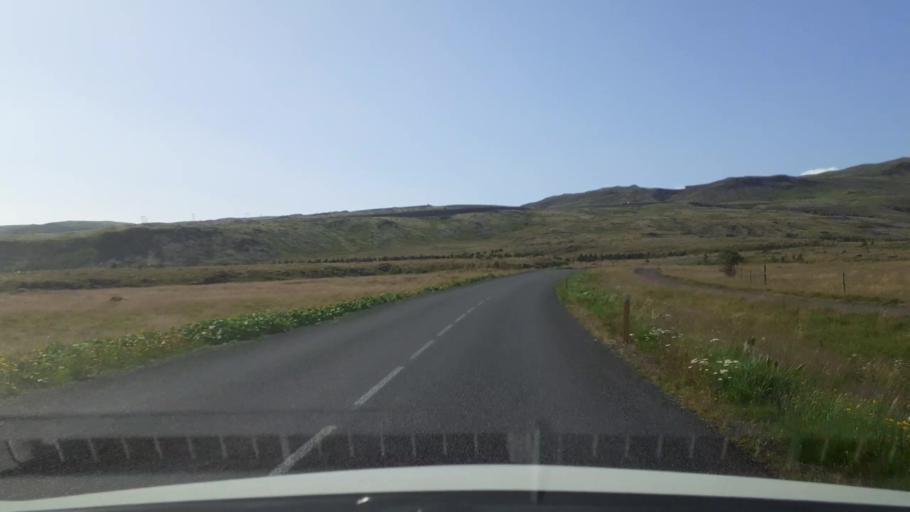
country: IS
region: South
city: Hveragerdi
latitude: 64.0132
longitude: -21.2007
